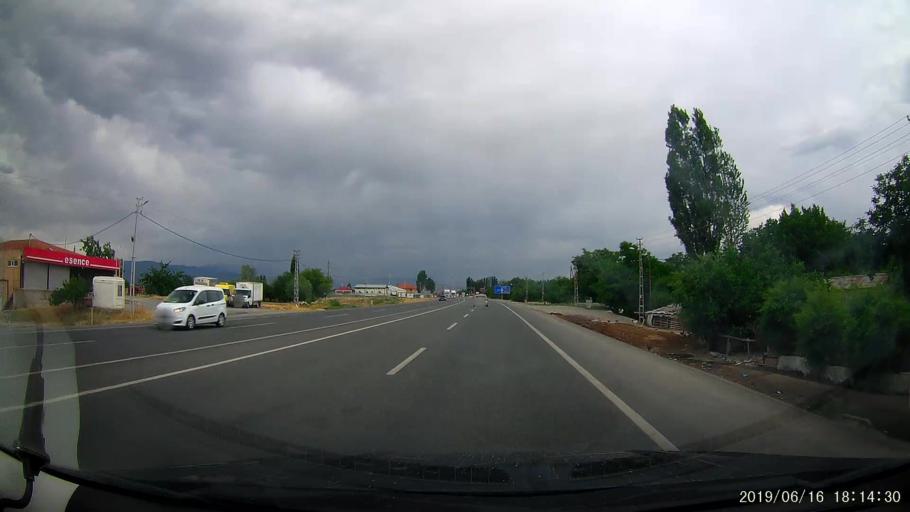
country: TR
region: Erzincan
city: Erzincan
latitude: 39.7243
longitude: 39.5575
